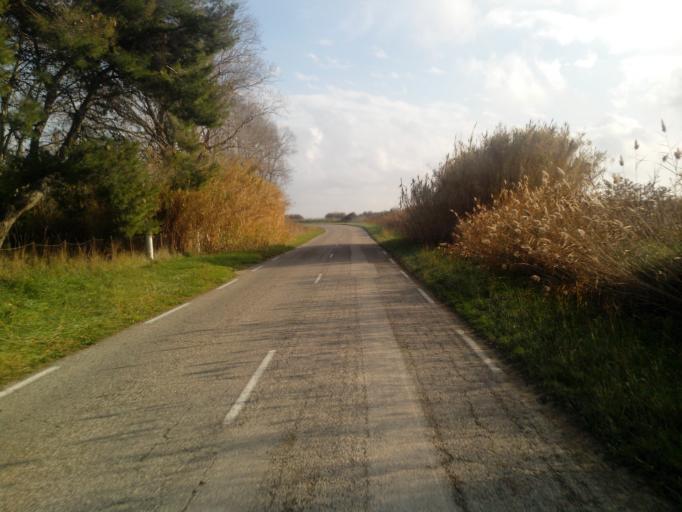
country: FR
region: Provence-Alpes-Cote d'Azur
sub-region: Departement des Bouches-du-Rhone
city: Arles
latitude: 43.5695
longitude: 4.5604
